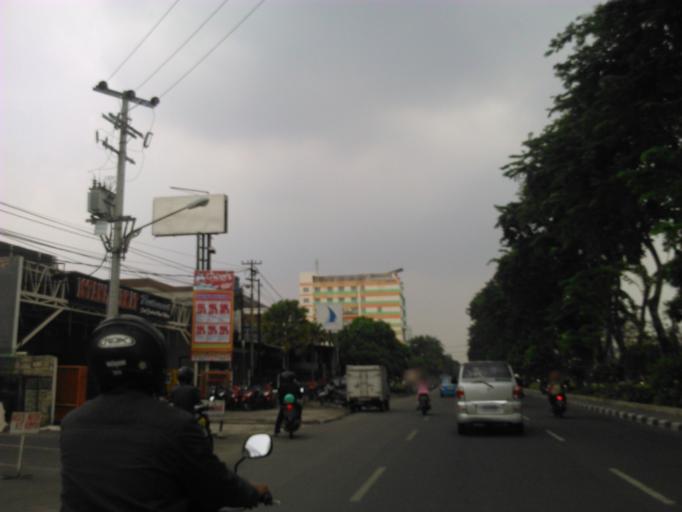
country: ID
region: East Java
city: Gubengairlangga
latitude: -7.2802
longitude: 112.7680
